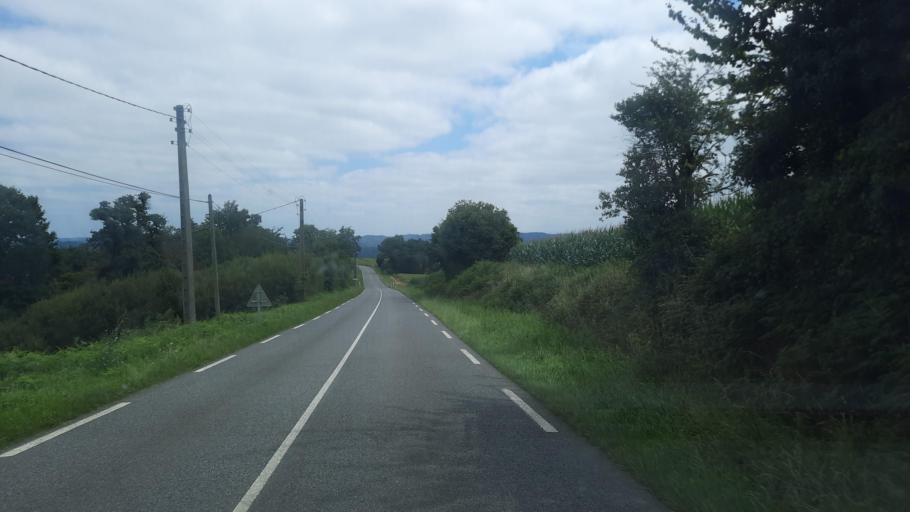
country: FR
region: Midi-Pyrenees
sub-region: Departement des Hautes-Pyrenees
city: Trie-sur-Baise
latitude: 43.3033
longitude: 0.3916
